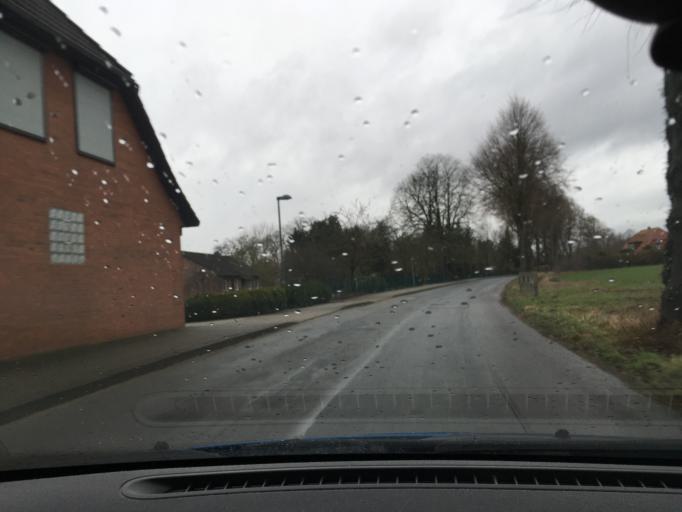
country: DE
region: Mecklenburg-Vorpommern
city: Nostorf
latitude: 53.3494
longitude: 10.6508
